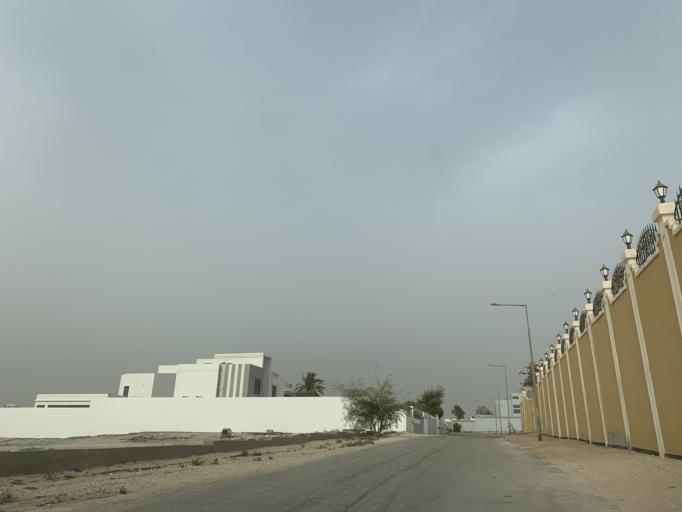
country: BH
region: Northern
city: Ar Rifa'
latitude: 26.1394
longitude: 50.5303
